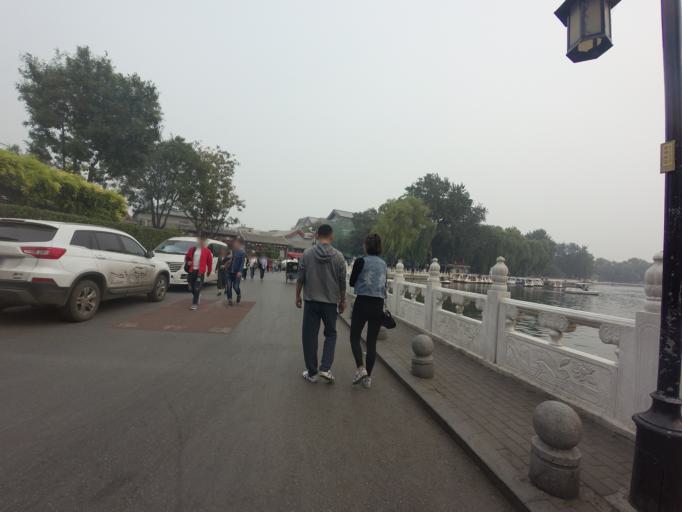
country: CN
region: Beijing
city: Jingshan
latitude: 39.9374
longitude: 116.3879
